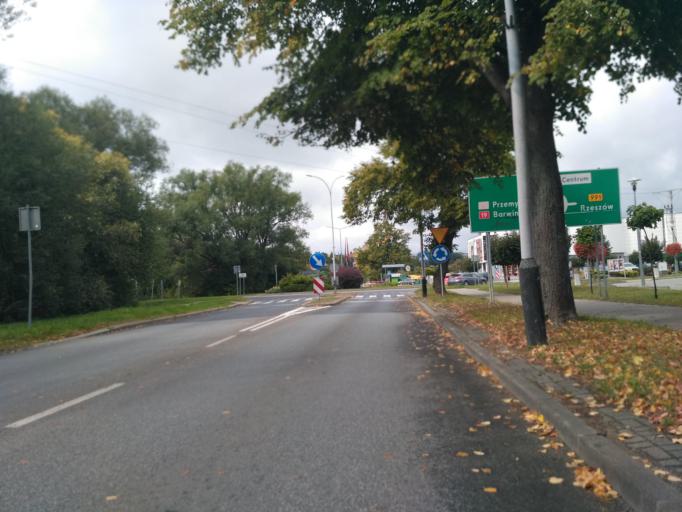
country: PL
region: Subcarpathian Voivodeship
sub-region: Krosno
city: Krosno
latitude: 49.6918
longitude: 21.7740
